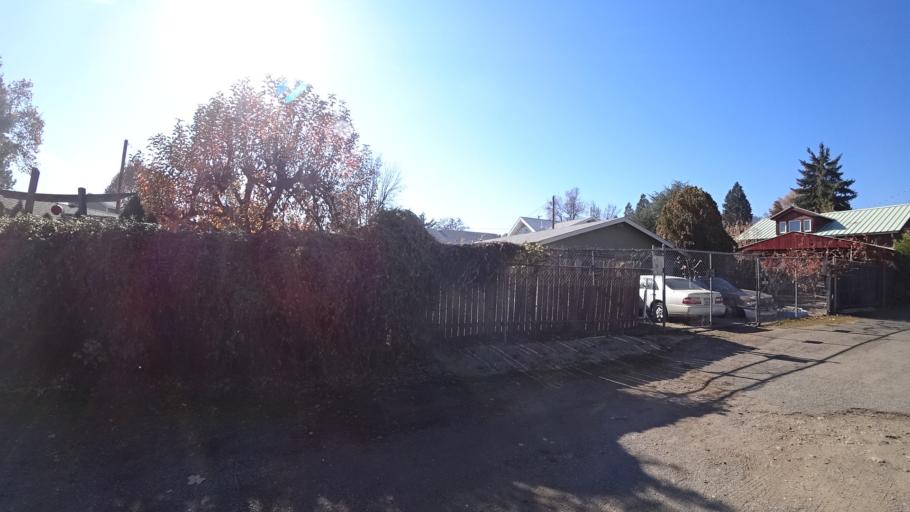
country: US
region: California
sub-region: Siskiyou County
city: Yreka
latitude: 41.7321
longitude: -122.6427
